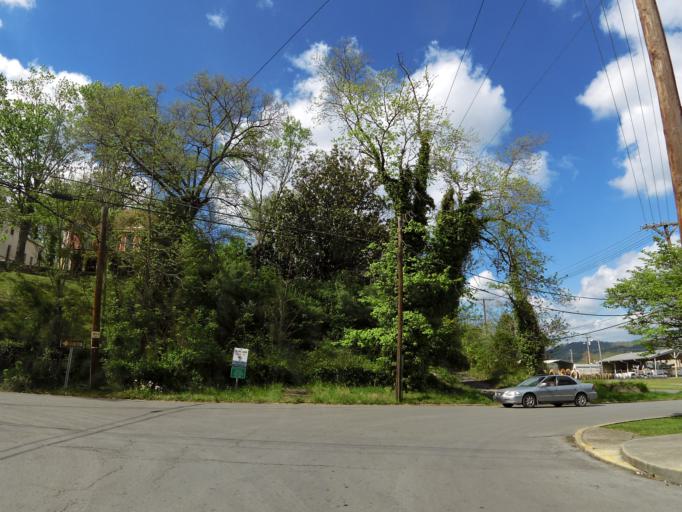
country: US
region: Kentucky
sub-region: Bell County
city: Middlesboro
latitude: 36.6097
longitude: -83.7145
